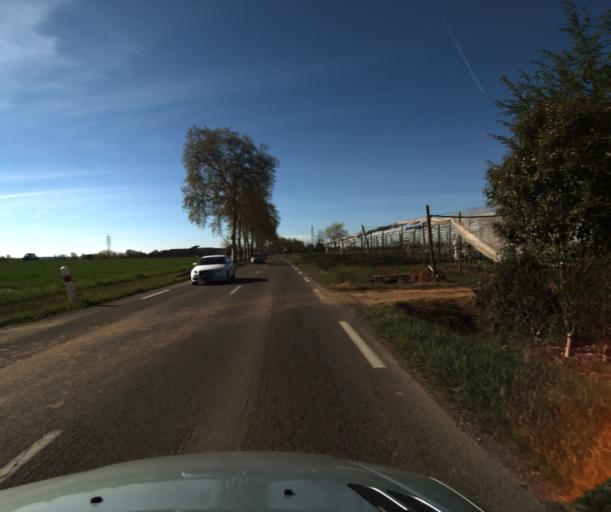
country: FR
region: Midi-Pyrenees
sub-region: Departement du Tarn-et-Garonne
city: Montbeton
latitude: 44.0392
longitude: 1.3071
